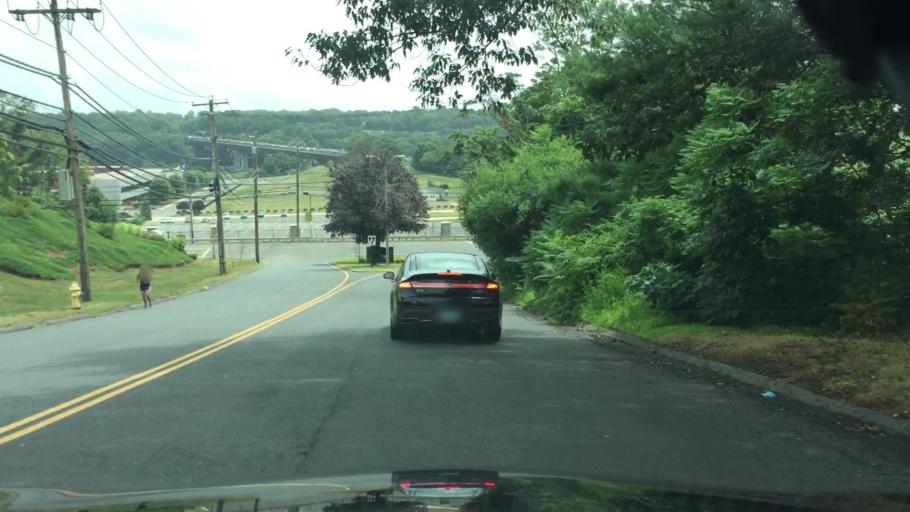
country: US
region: Connecticut
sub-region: New Haven County
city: City of Milford (balance)
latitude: 41.2485
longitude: -73.1028
